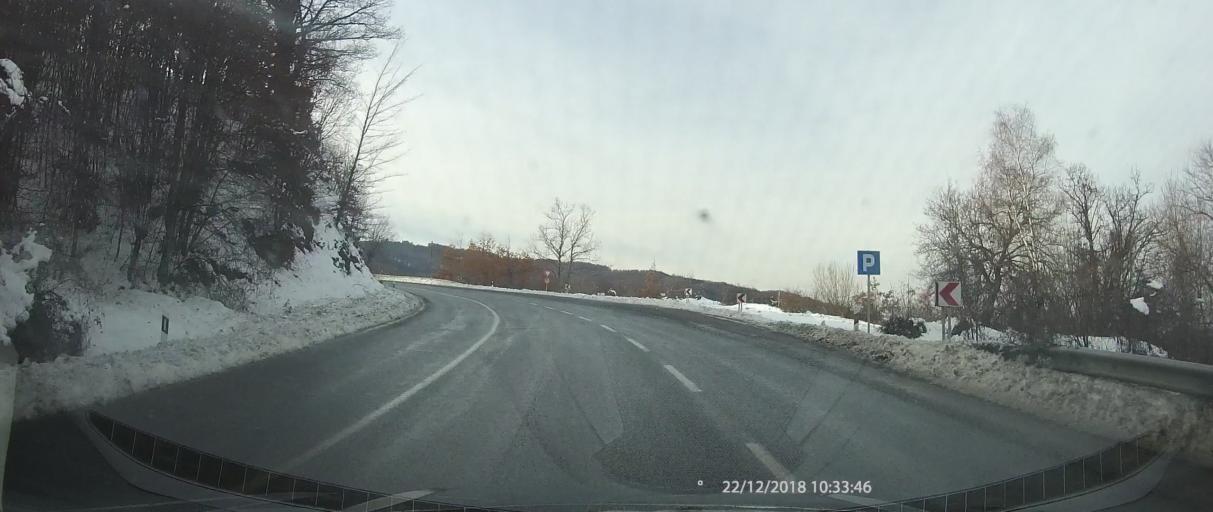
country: MK
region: Kriva Palanka
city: Kriva Palanka
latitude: 42.2198
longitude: 22.4453
